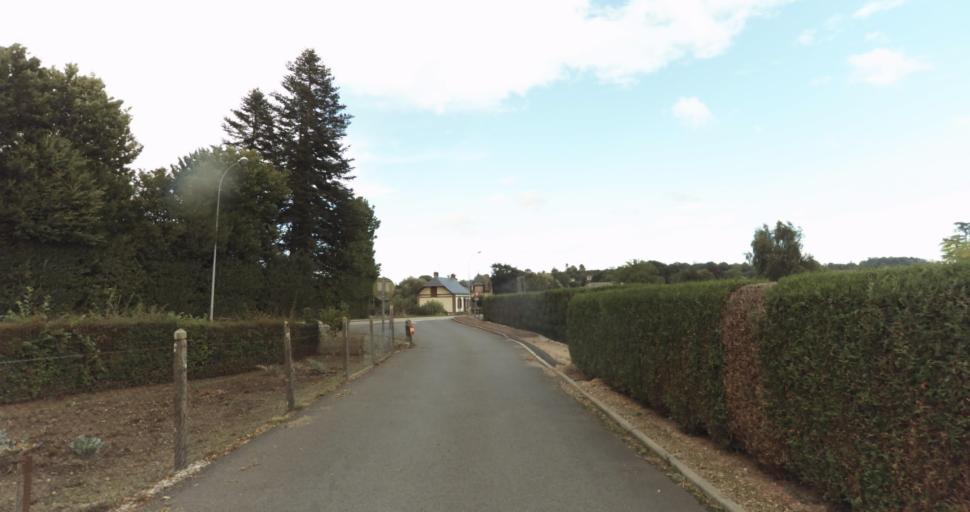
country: FR
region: Lower Normandy
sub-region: Departement de l'Orne
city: Sainte-Gauburge-Sainte-Colombe
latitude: 48.7188
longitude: 0.4285
